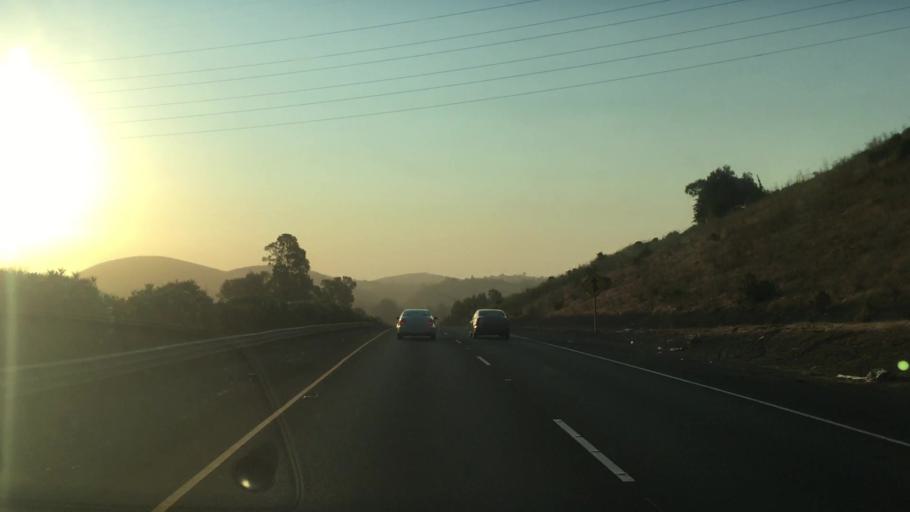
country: US
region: California
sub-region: Contra Costa County
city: Crockett
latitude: 38.0855
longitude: -122.2094
